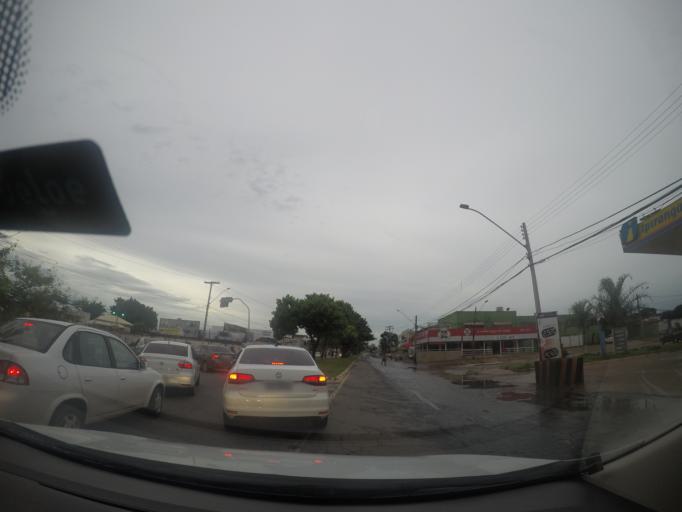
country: BR
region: Goias
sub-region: Goiania
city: Goiania
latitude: -16.6336
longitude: -49.2365
